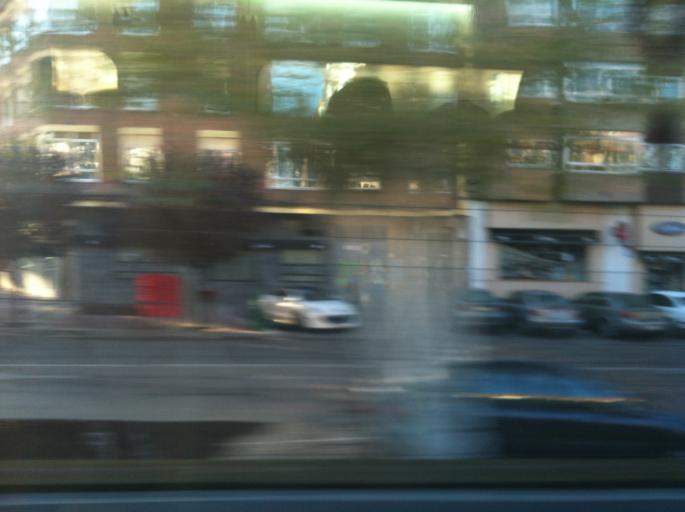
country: ES
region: Castille and Leon
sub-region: Provincia de Valladolid
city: Valladolid
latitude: 41.6467
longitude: -4.7141
